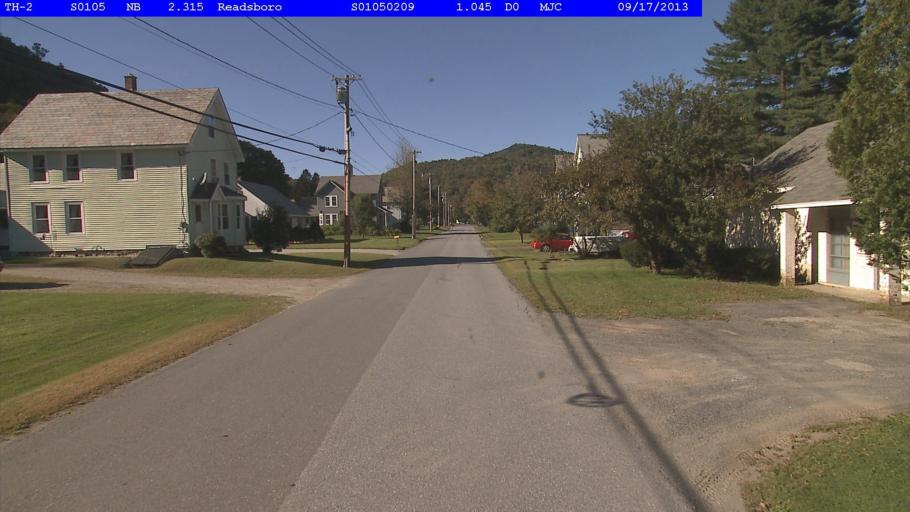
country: US
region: Massachusetts
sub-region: Franklin County
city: Charlemont
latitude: 42.7647
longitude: -72.9451
